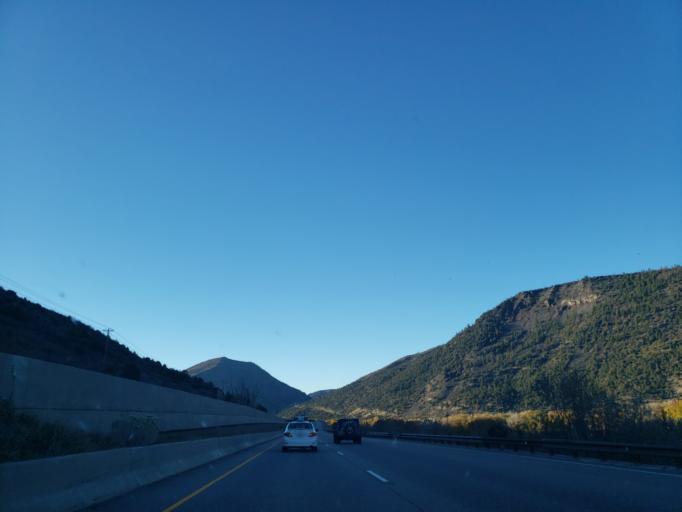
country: US
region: Colorado
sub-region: Pitkin County
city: Snowmass Village
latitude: 39.2860
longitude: -106.9054
